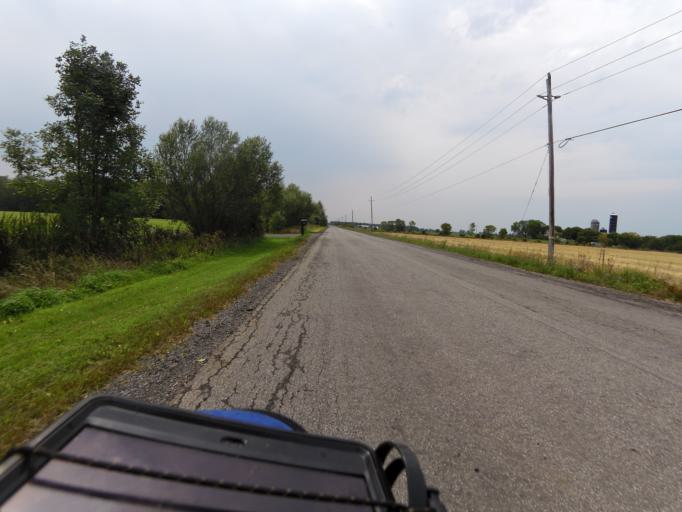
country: CA
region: Ontario
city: Casselman
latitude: 45.1742
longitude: -75.3723
